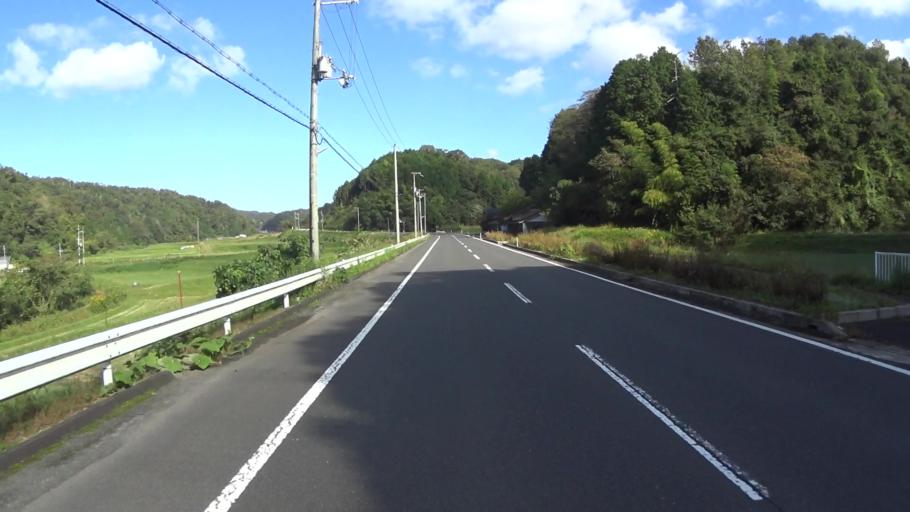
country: JP
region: Kyoto
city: Miyazu
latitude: 35.6027
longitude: 135.1385
